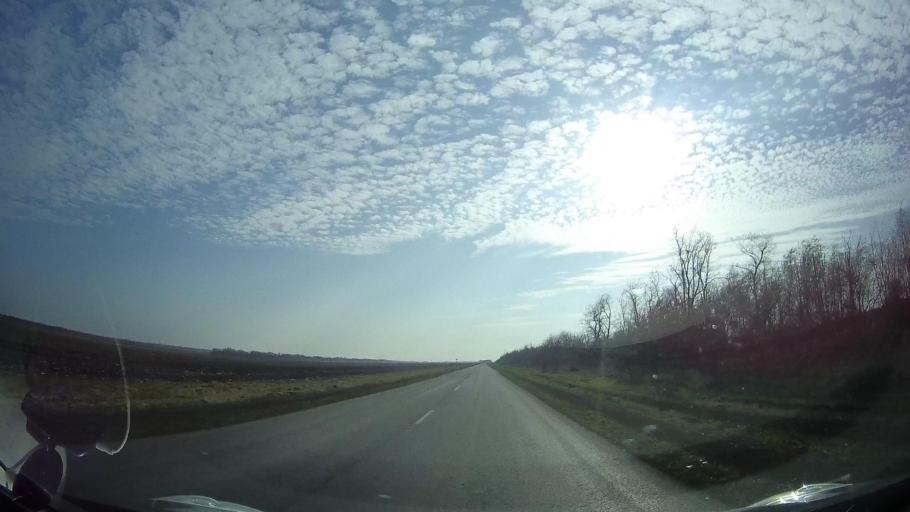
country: RU
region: Rostov
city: Veselyy
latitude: 46.9767
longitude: 40.7198
